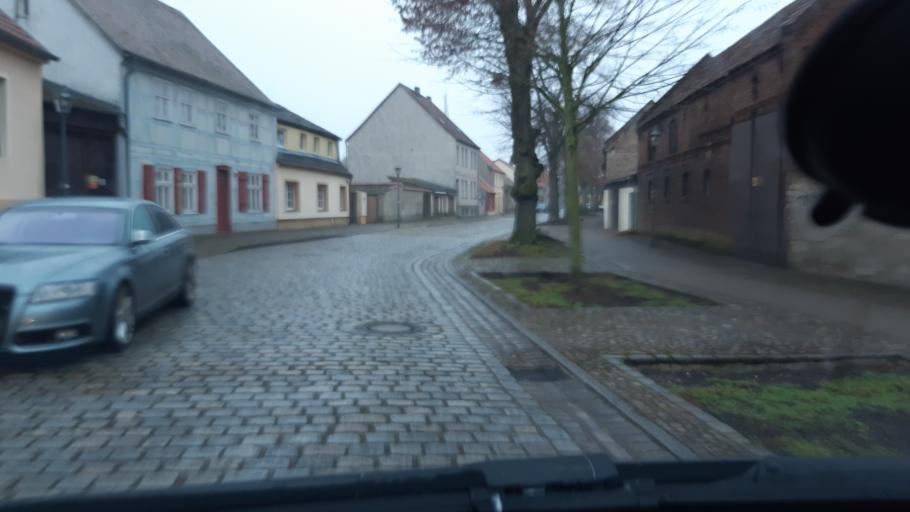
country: DE
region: Brandenburg
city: Kremmen
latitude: 52.7609
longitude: 13.0288
